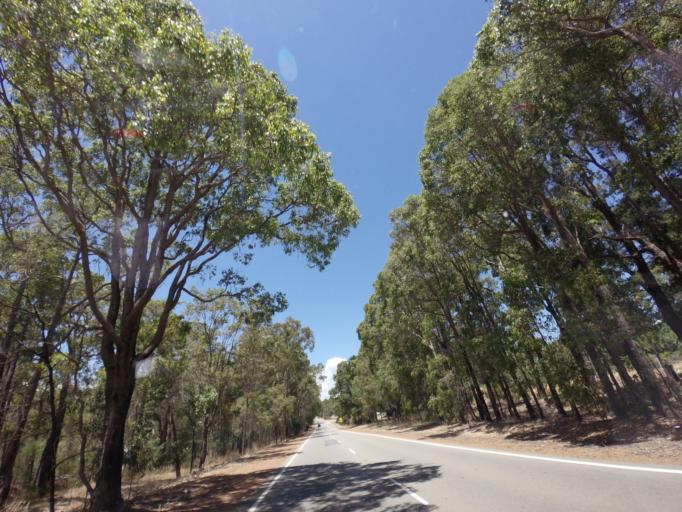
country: AU
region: Western Australia
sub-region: Mundaring
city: Parkerville
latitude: -31.9002
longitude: 116.1326
